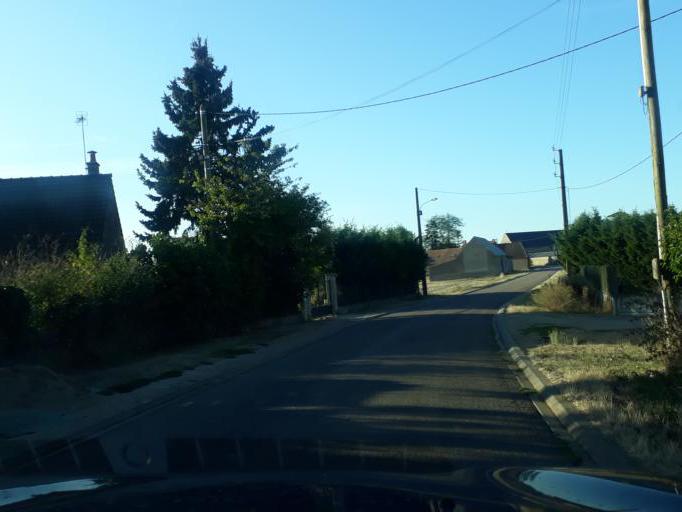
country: FR
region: Centre
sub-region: Departement du Loiret
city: Epieds-en-Beauce
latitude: 47.9451
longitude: 1.5705
